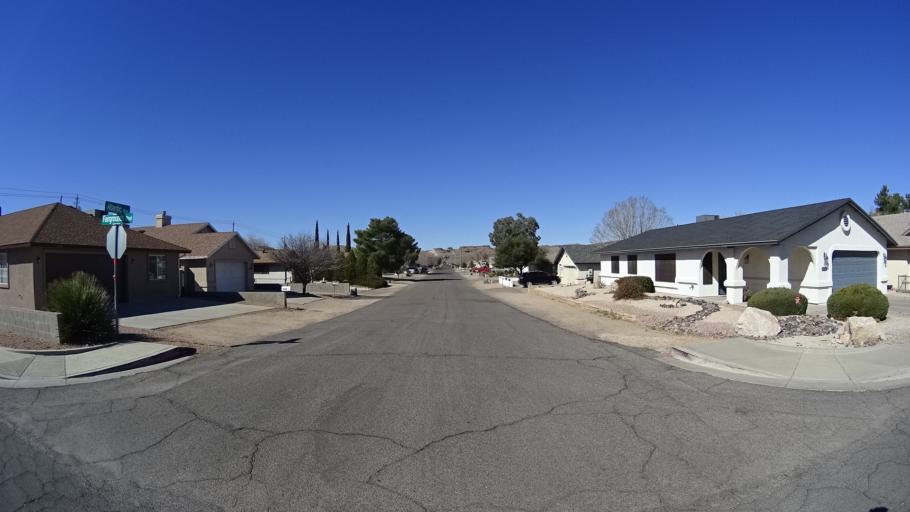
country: US
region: Arizona
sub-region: Mohave County
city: Kingman
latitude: 35.2112
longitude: -114.0291
